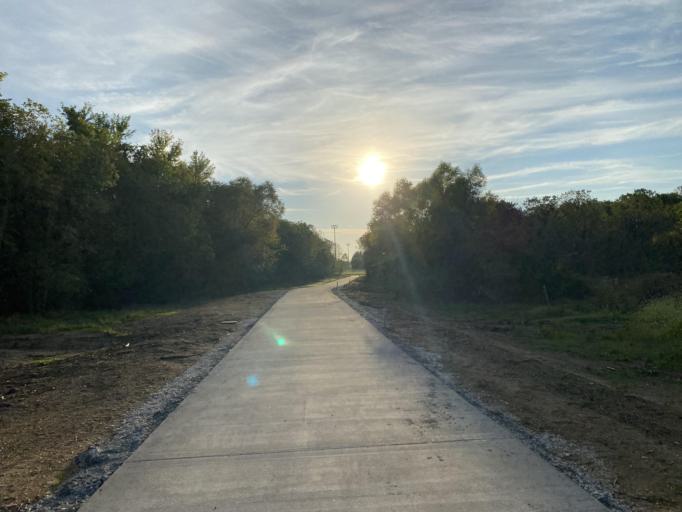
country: US
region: Arkansas
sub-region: Washington County
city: Johnson
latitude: 36.1036
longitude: -94.2029
